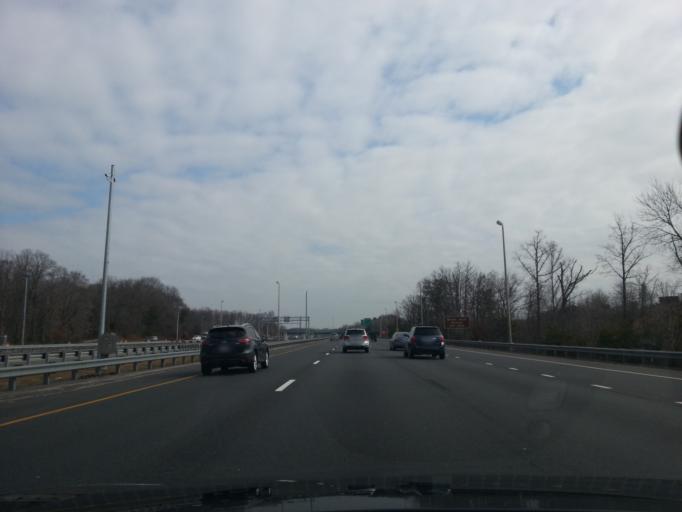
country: US
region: Virginia
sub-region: Prince William County
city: Dumfries
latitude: 38.5750
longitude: -77.3277
